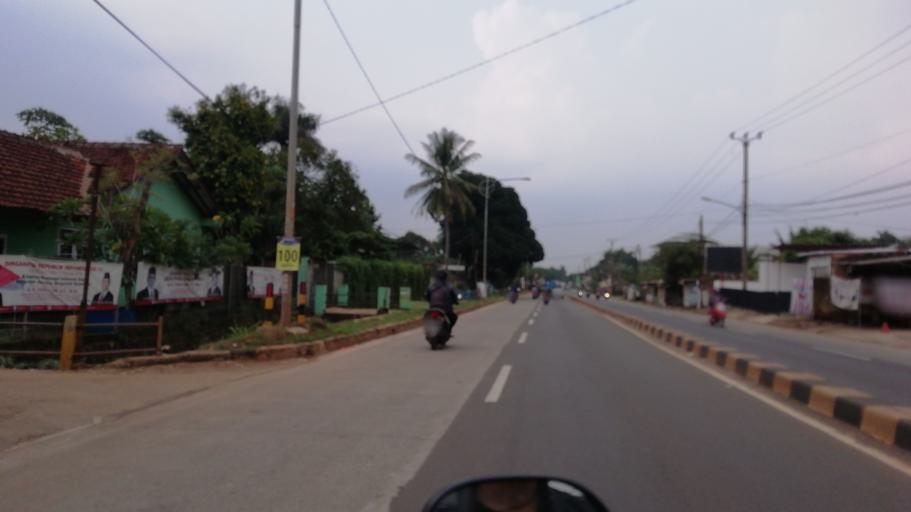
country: ID
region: West Java
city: Parung
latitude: -6.4697
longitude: 106.7292
